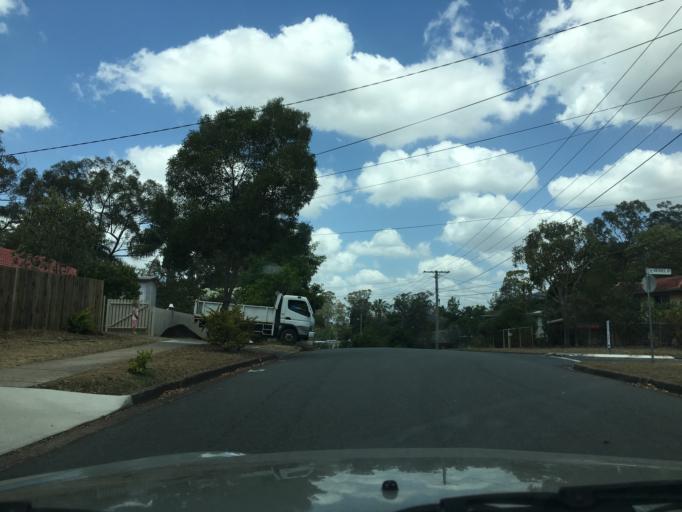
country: AU
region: Queensland
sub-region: Logan
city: Logan City
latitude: -27.6588
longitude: 153.1042
